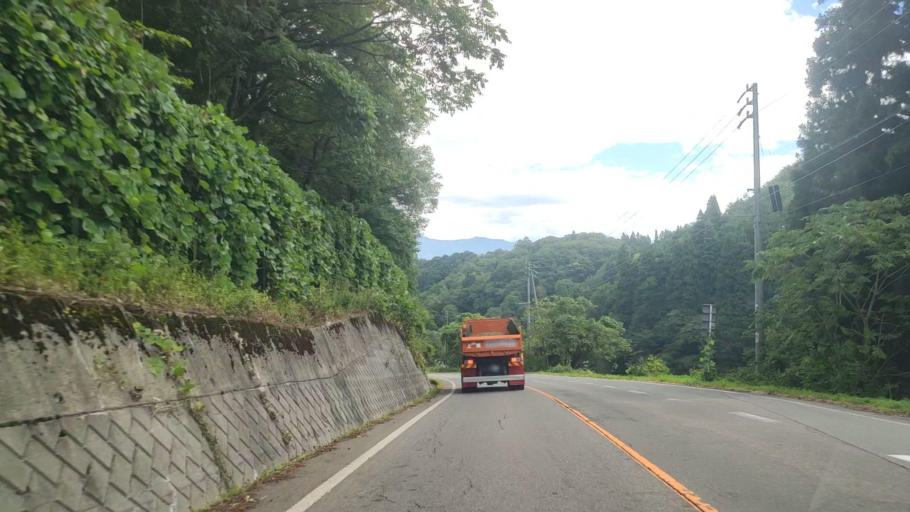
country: JP
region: Nagano
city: Iiyama
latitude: 36.8667
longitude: 138.3358
